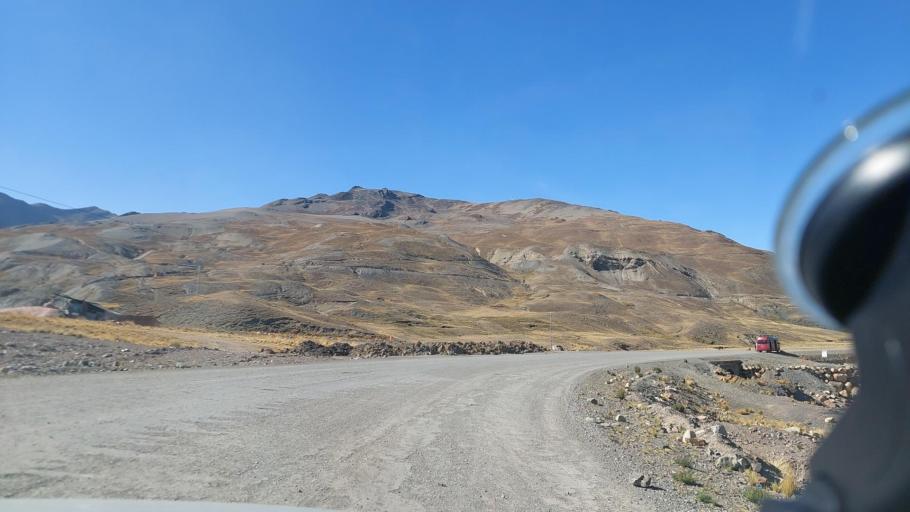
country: BO
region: La Paz
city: La Paz
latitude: -16.3934
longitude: -68.1053
